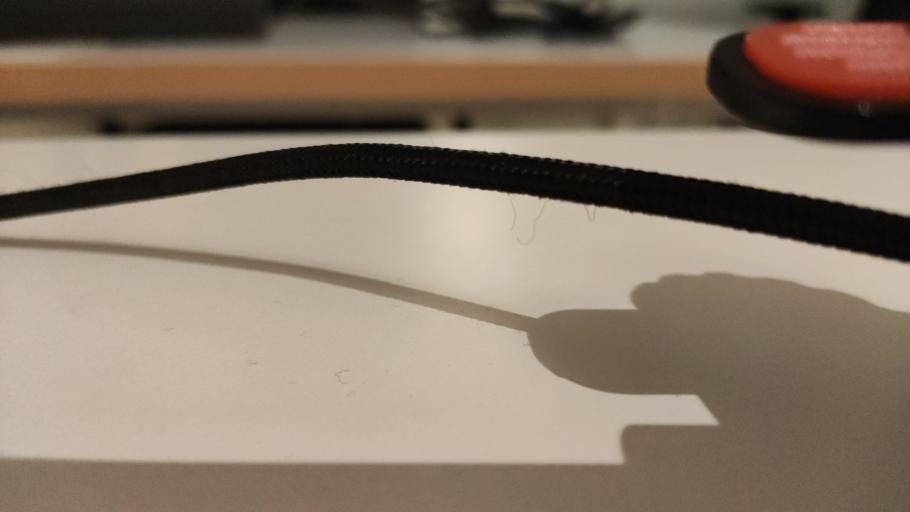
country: RU
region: Moskovskaya
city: Malaya Dubna
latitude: 55.8558
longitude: 38.9624
